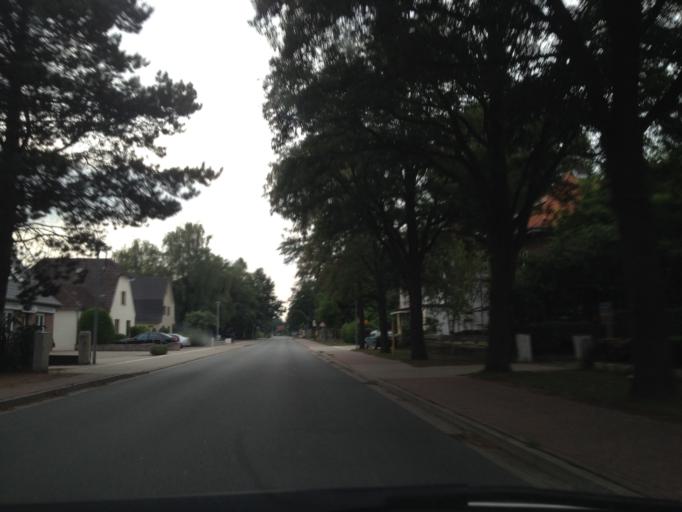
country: DE
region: Schleswig-Holstein
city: Rickling
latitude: 54.0026
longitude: 10.1670
